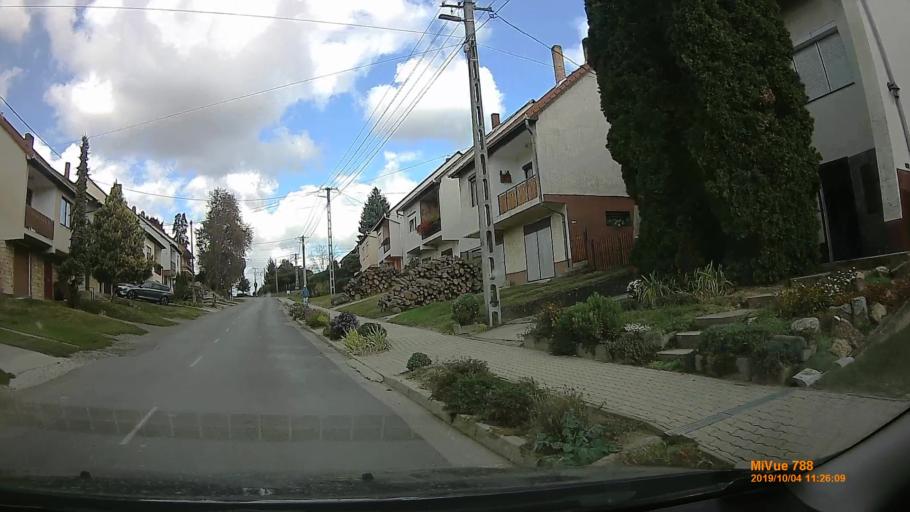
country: HU
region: Somogy
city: Kaposvar
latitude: 46.5076
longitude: 17.8158
